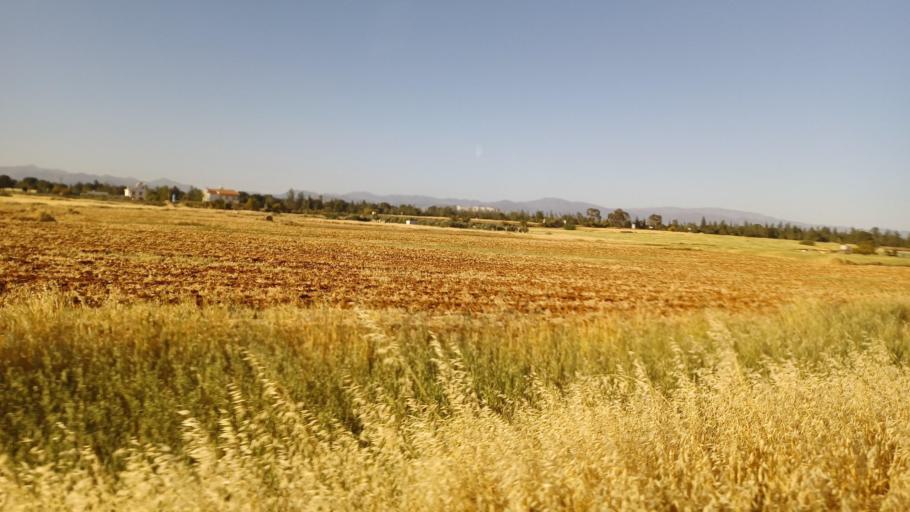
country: CY
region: Lefkosia
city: Kokkinotrimithia
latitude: 35.1498
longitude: 33.1796
